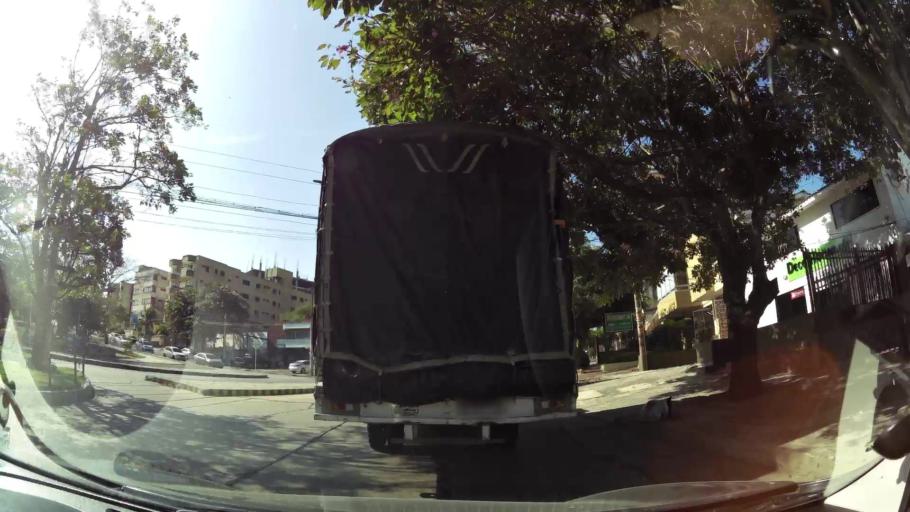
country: CO
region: Atlantico
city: Barranquilla
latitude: 10.9947
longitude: -74.8193
